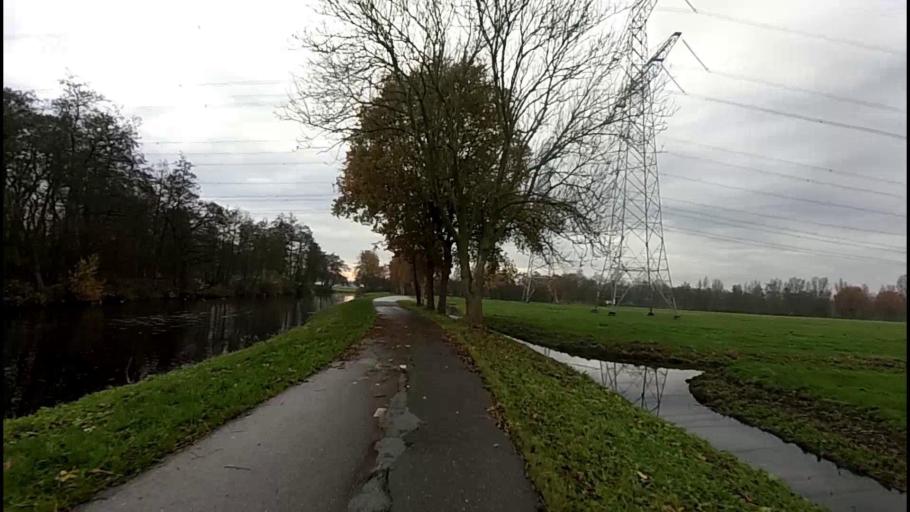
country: NL
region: South Holland
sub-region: Gemeente Krimpen aan den IJssel
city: Krimpen aan den IJssel
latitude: 51.9142
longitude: 4.6447
